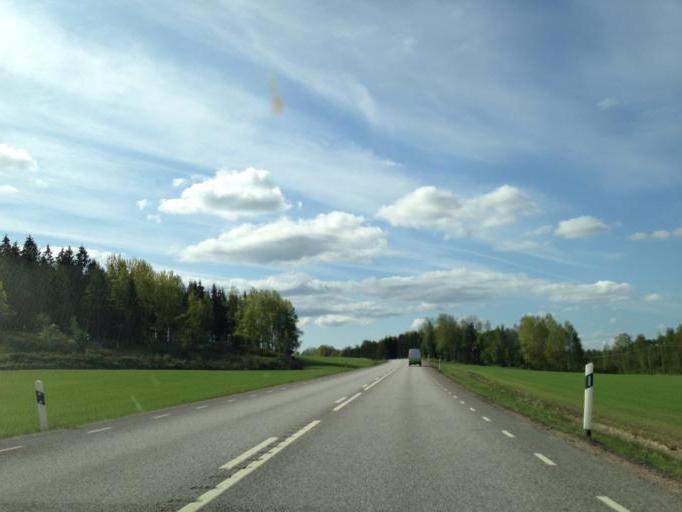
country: SE
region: Soedermanland
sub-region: Nykopings Kommun
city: Svalsta
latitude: 58.8373
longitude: 16.9232
